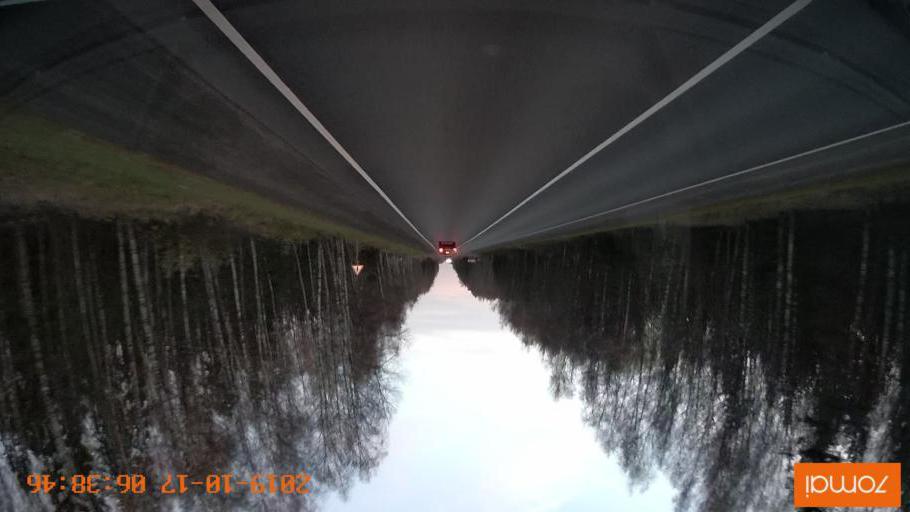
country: RU
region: Ivanovo
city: Novoye Leushino
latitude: 56.6516
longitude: 40.5845
